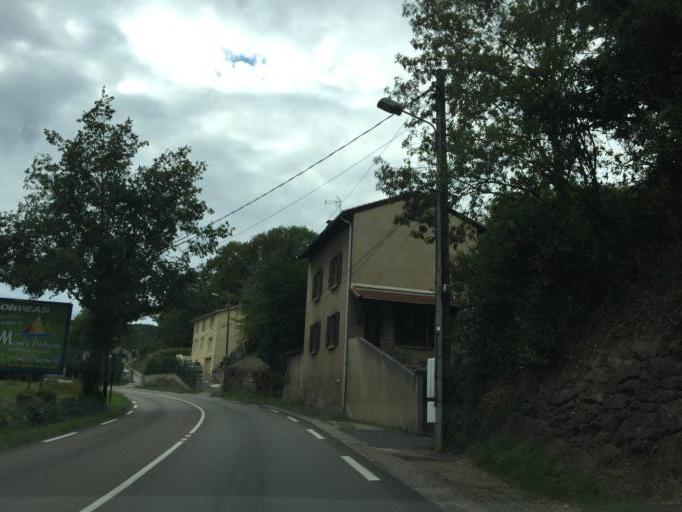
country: FR
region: Rhone-Alpes
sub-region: Departement de la Loire
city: Saint-Chamond
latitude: 45.4720
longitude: 4.4896
